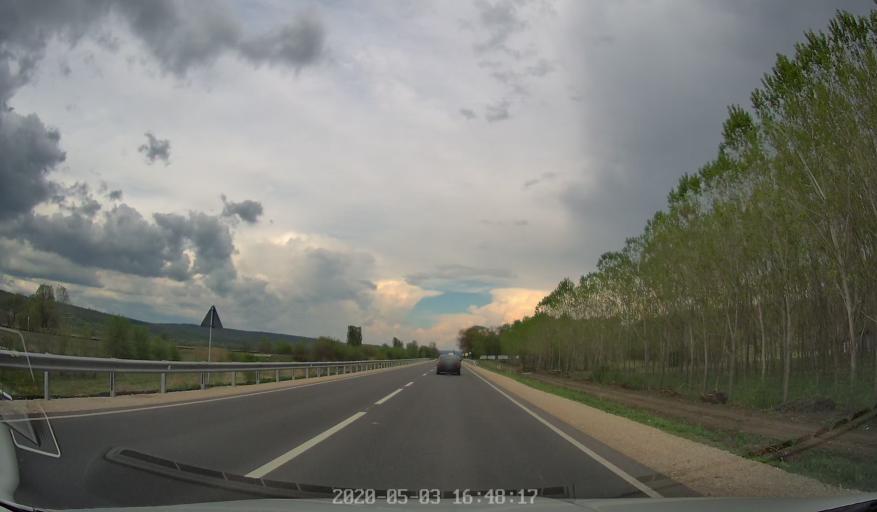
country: MD
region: Stinga Nistrului
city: Bucovat
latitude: 47.1799
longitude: 28.4939
